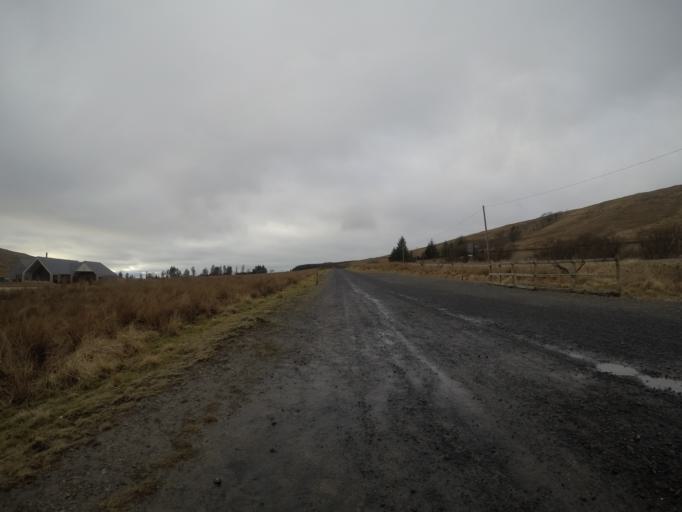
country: GB
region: Scotland
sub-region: North Ayrshire
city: Fairlie
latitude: 55.7787
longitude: -4.8039
